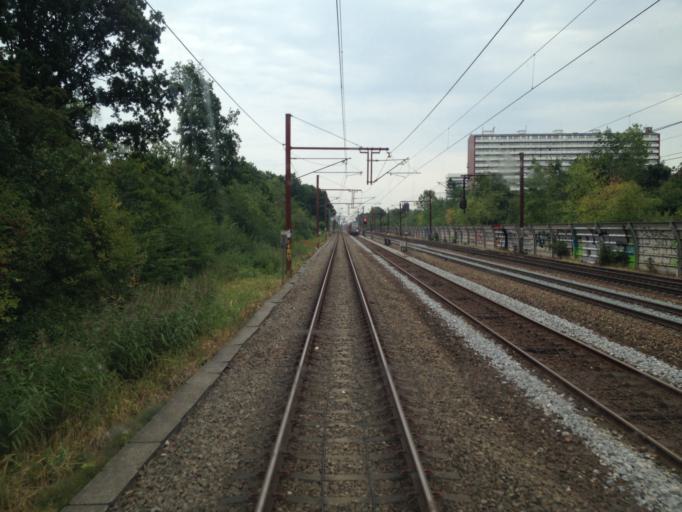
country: DK
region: Capital Region
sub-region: Rodovre Kommune
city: Rodovre
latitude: 55.6649
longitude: 12.4485
